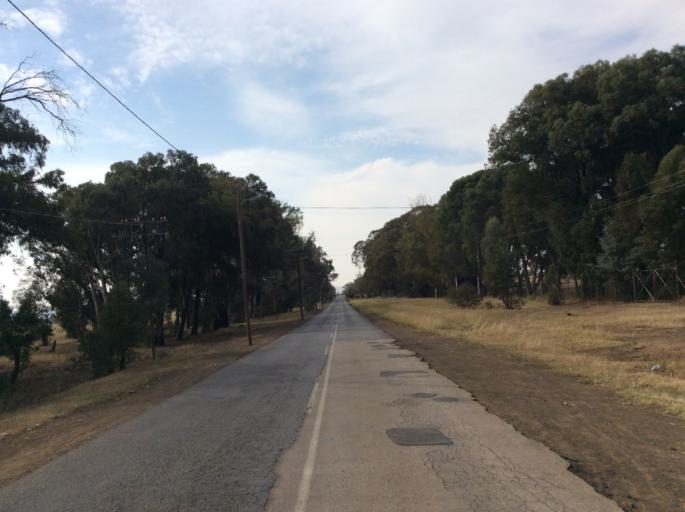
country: ZA
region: Orange Free State
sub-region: Xhariep District Municipality
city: Dewetsdorp
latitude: -29.5775
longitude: 26.6758
